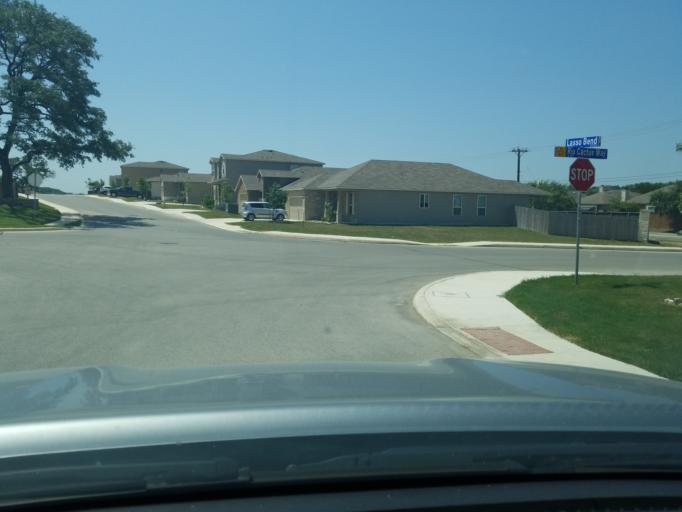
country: US
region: Texas
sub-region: Bexar County
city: Timberwood Park
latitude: 29.7073
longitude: -98.4831
